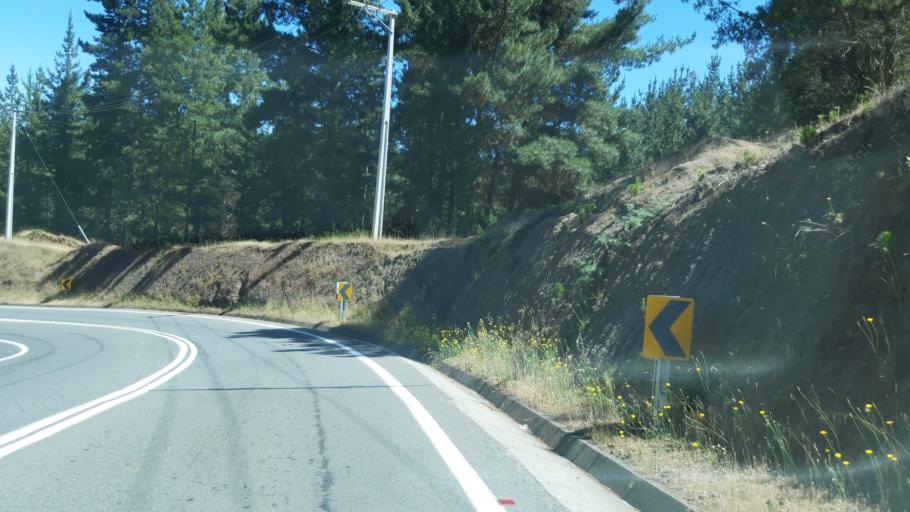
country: CL
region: Maule
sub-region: Provincia de Talca
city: Talca
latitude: -34.9790
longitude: -71.9696
